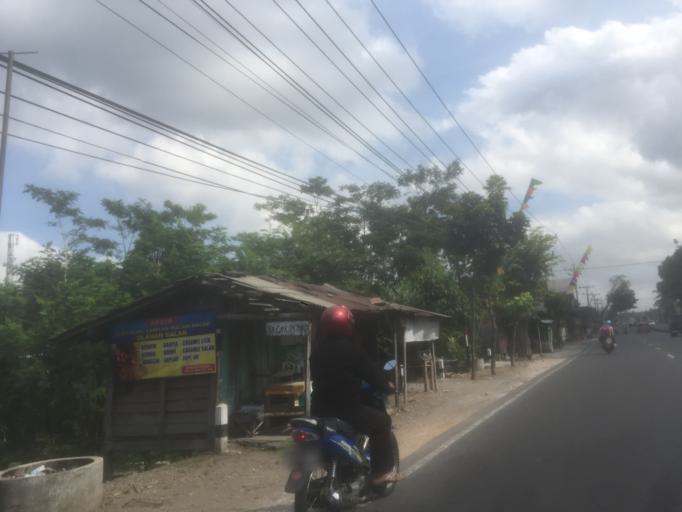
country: ID
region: Daerah Istimewa Yogyakarta
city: Sleman
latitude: -7.6789
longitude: 110.3379
